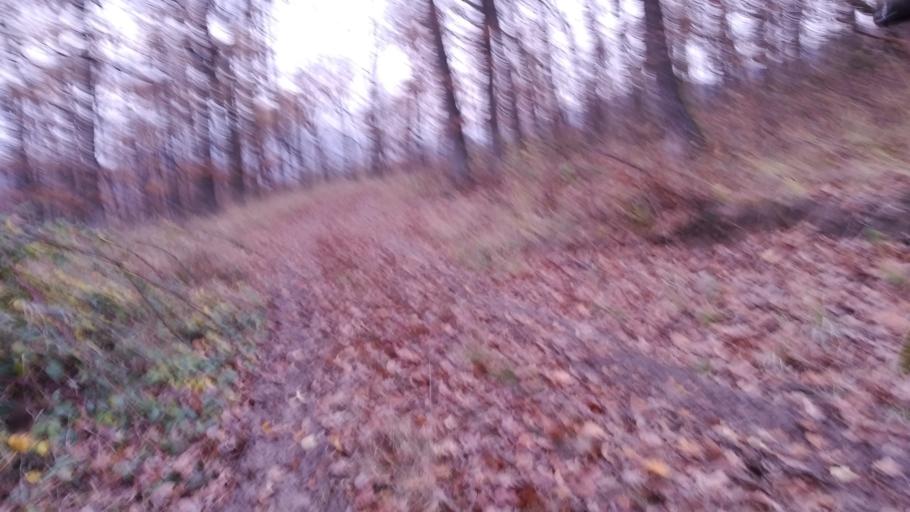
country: HU
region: Pest
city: Csobanka
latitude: 47.6775
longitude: 18.9564
